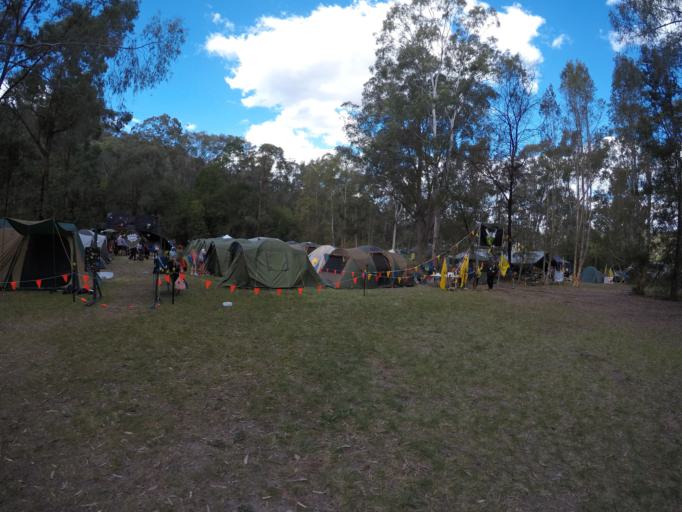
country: AU
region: New South Wales
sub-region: Hawkesbury
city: Pitt Town
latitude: -33.4703
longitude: 150.8912
